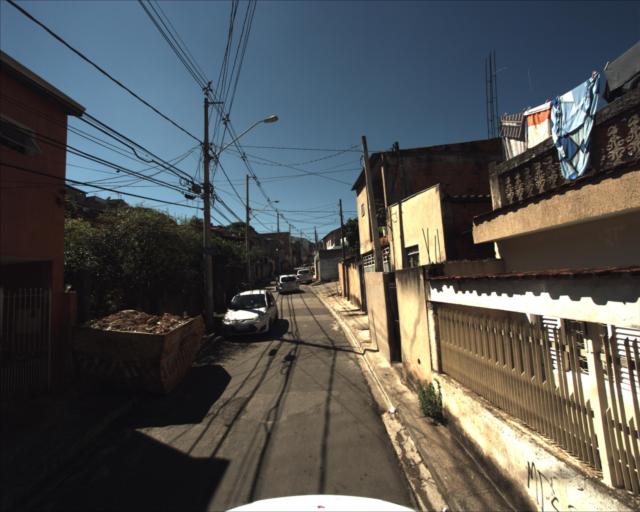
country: BR
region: Sao Paulo
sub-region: Votorantim
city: Votorantim
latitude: -23.5220
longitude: -47.4345
